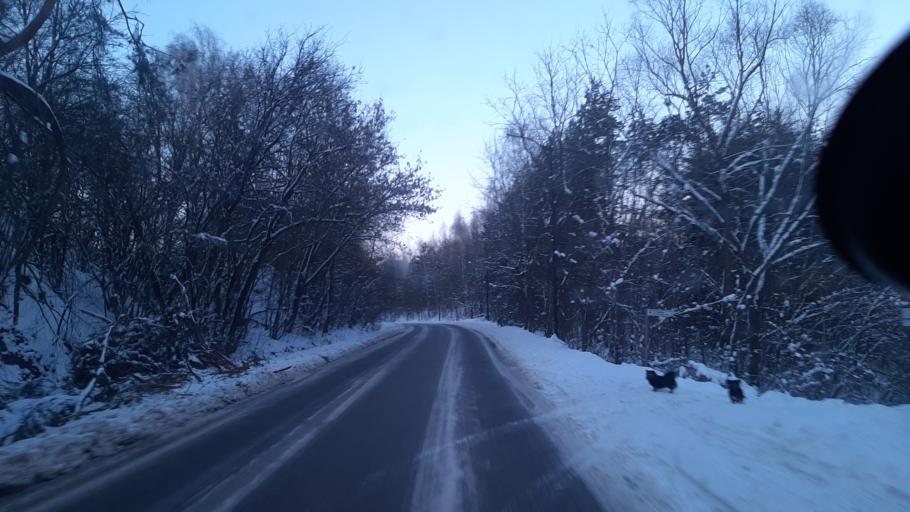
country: PL
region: Lublin Voivodeship
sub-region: Powiat lubelski
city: Lublin
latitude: 51.3175
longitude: 22.5610
